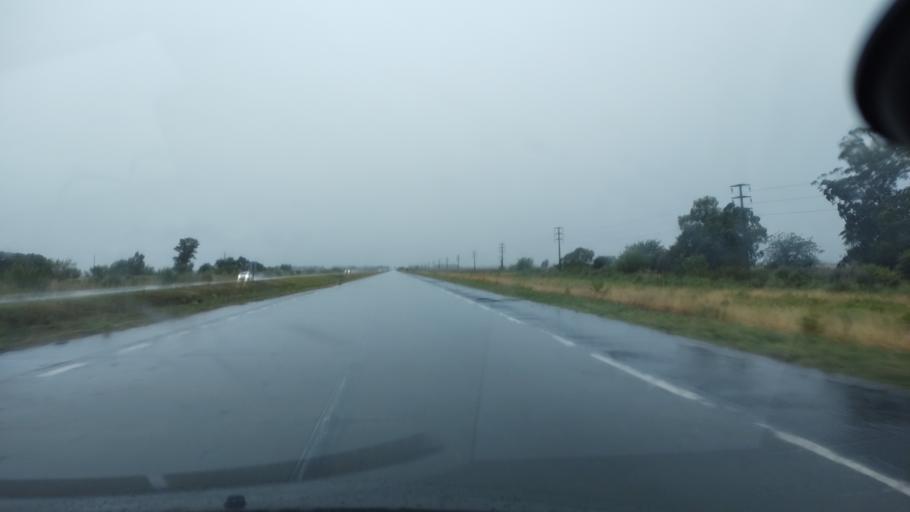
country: AR
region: Buenos Aires
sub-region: Partido de San Vicente
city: San Vicente
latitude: -35.0653
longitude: -58.4793
